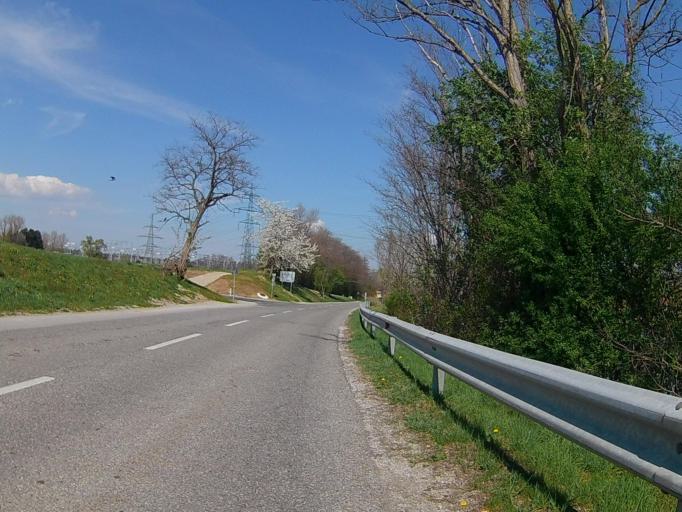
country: SI
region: Miklavz na Dravskem Polju
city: Miklavz na Dravskem Polju
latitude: 46.5164
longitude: 15.7001
